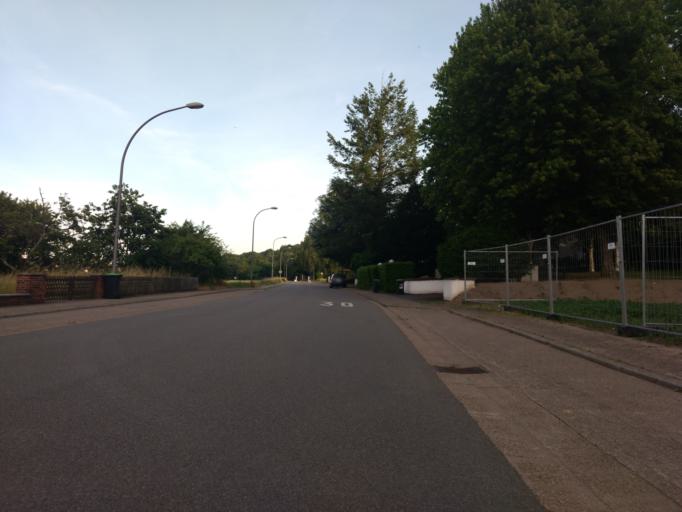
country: DE
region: Saarland
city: Wallerfangen
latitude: 49.3088
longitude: 6.7251
